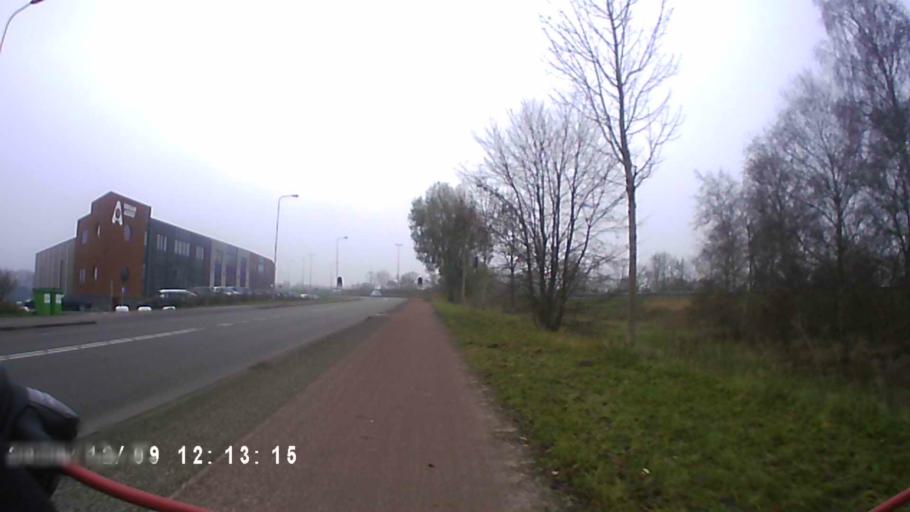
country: NL
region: Groningen
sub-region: Gemeente Groningen
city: Oosterpark
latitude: 53.2029
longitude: 6.6055
